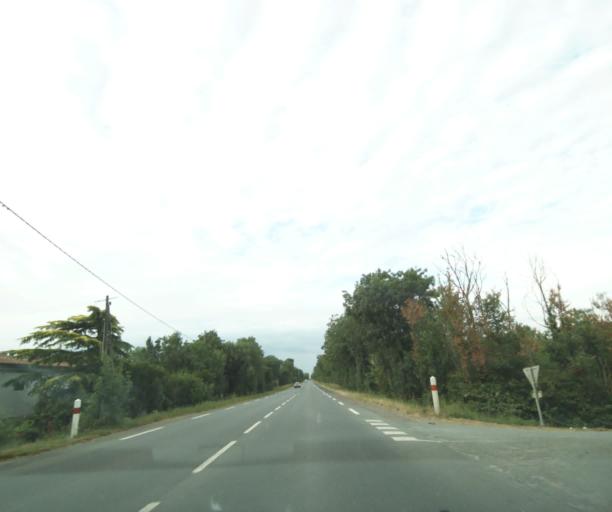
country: FR
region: Poitou-Charentes
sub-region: Departement de la Charente-Maritime
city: Andilly
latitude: 46.2678
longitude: -1.0059
